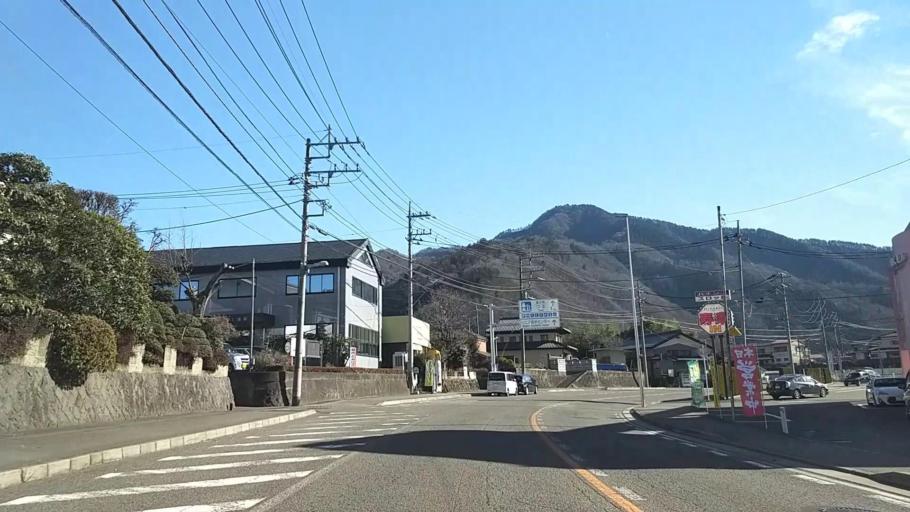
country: JP
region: Yamanashi
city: Otsuki
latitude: 35.5903
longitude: 138.9319
